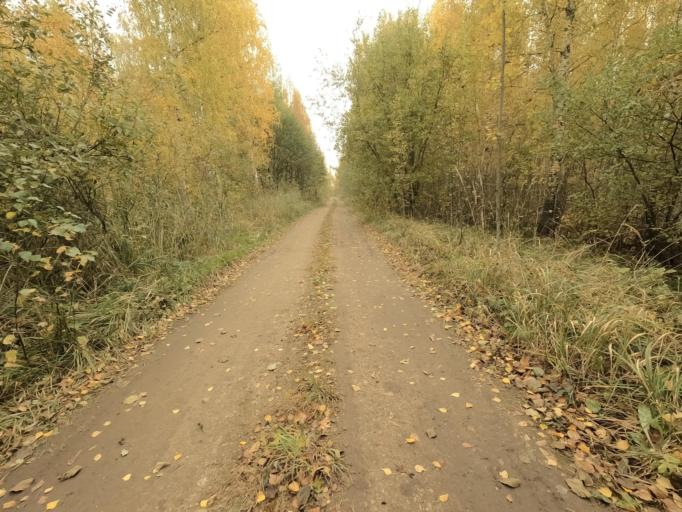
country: RU
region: Novgorod
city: Pankovka
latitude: 58.8738
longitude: 30.8846
